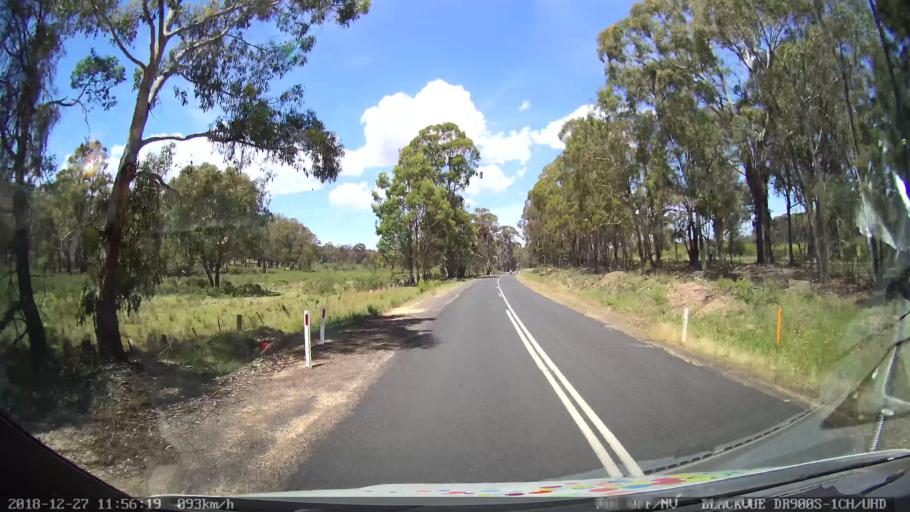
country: AU
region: New South Wales
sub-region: Blayney
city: Blayney
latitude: -33.6971
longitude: 149.3928
